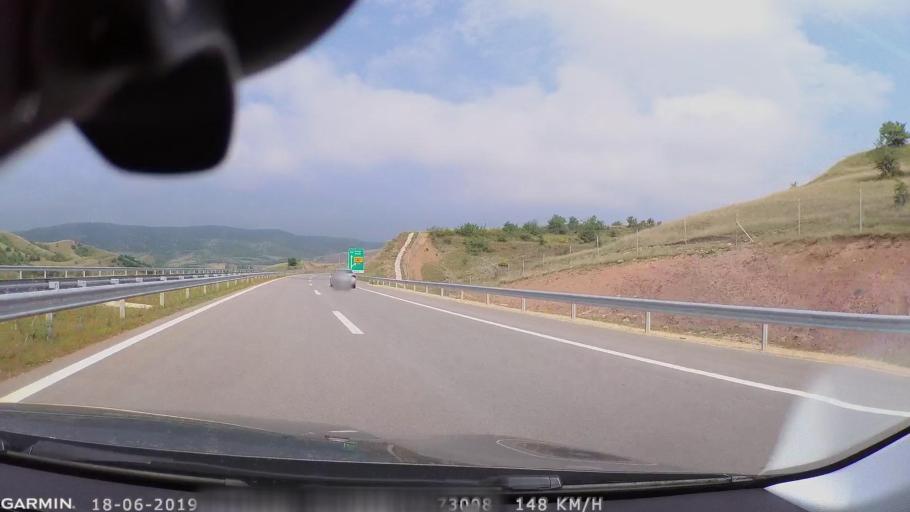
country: MK
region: Sveti Nikole
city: Gorobinci
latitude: 41.9301
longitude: 21.8285
